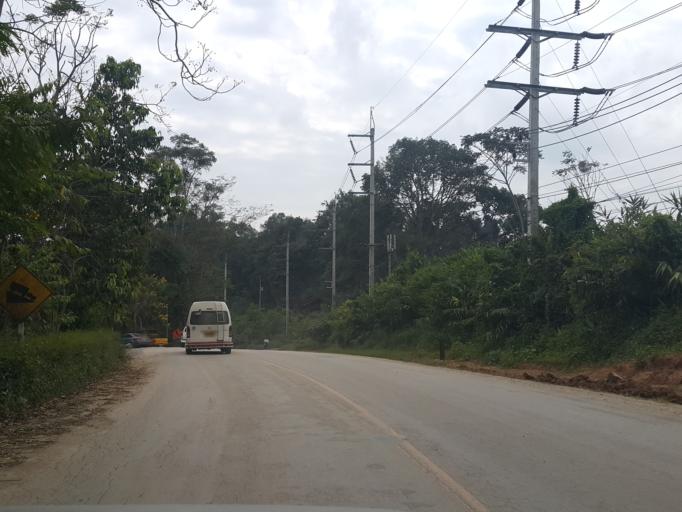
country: TH
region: Chiang Mai
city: Mae Taeng
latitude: 19.1334
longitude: 98.7038
